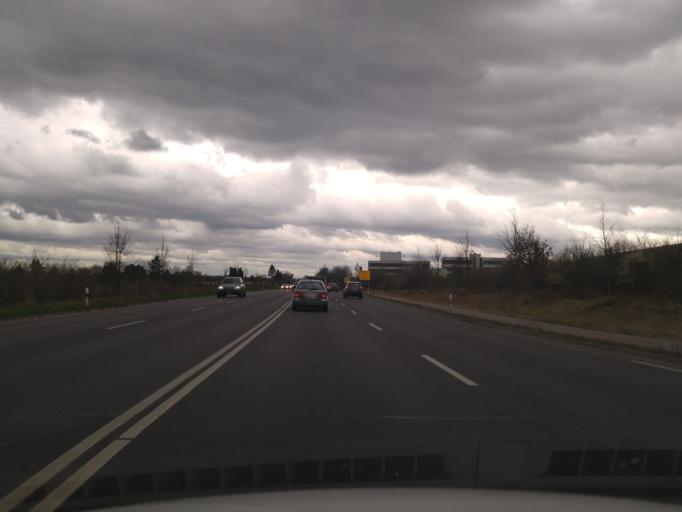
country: DE
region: North Rhine-Westphalia
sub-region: Regierungsbezirk Dusseldorf
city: Dusseldorf
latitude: 51.1613
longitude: 6.7720
